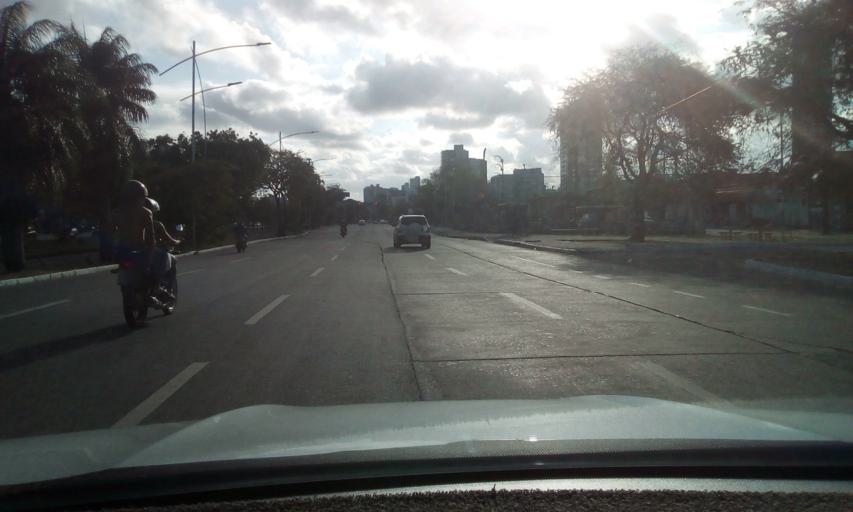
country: BR
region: Pernambuco
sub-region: Recife
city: Recife
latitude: -8.0399
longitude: -34.8796
